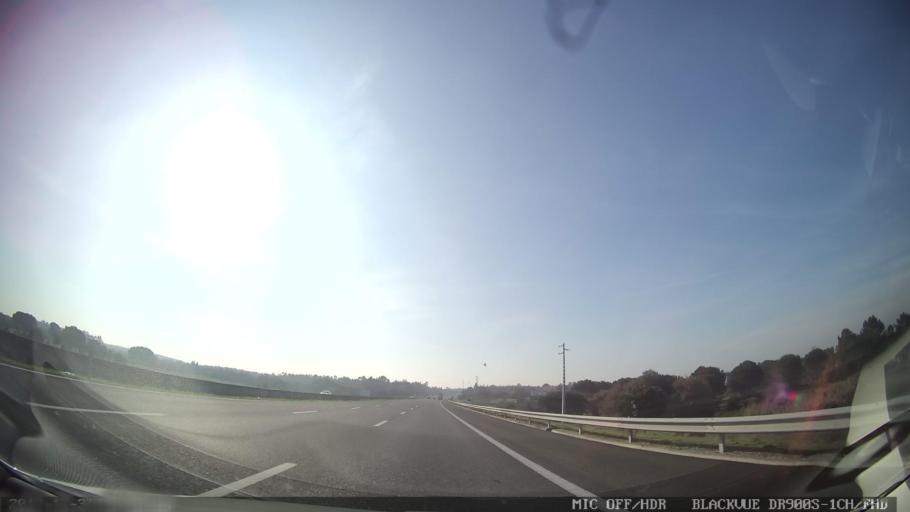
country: PT
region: Santarem
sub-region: Cartaxo
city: Cartaxo
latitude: 39.2120
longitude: -8.7797
